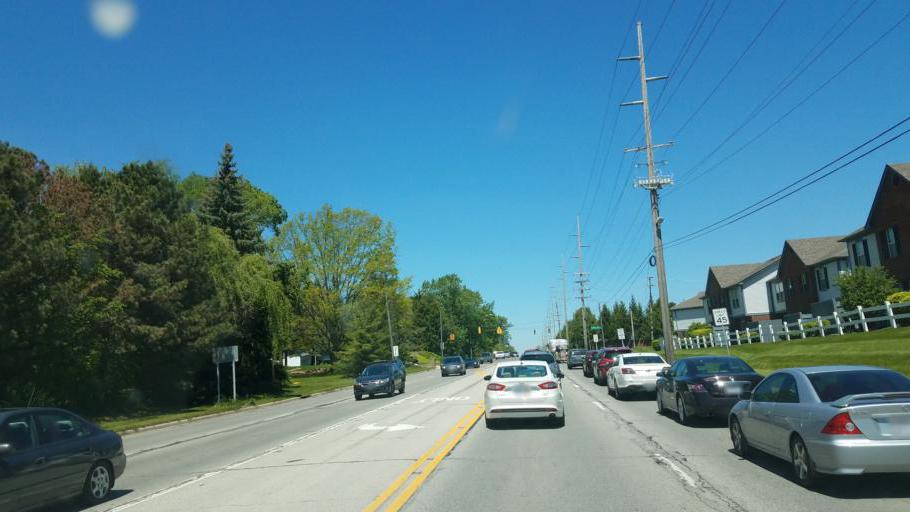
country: US
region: Ohio
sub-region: Delaware County
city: Powell
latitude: 40.1317
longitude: -83.0897
